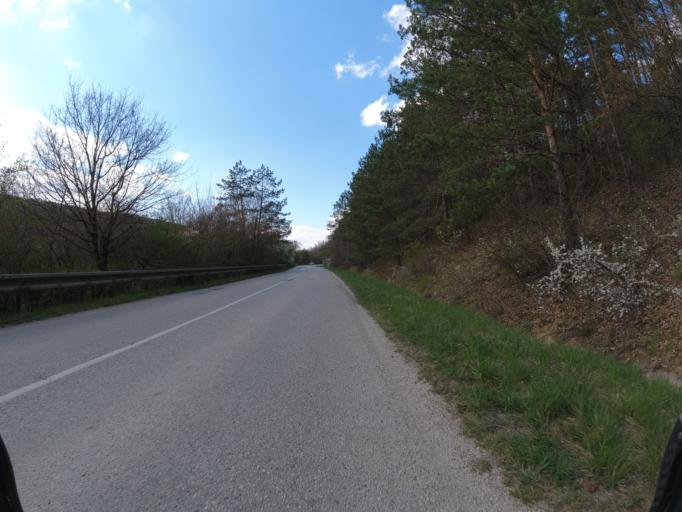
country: SK
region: Nitriansky
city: Stara Tura
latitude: 48.7561
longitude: 17.7164
